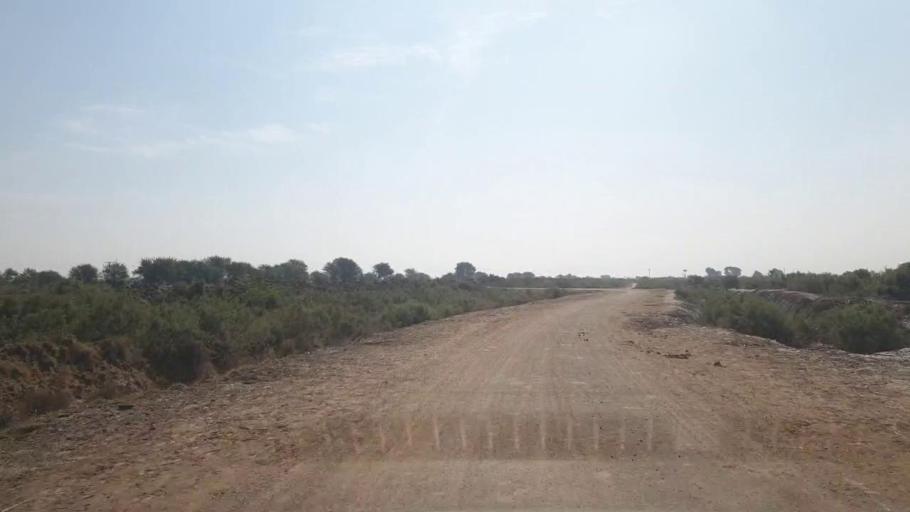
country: PK
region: Sindh
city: Mirwah Gorchani
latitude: 25.3657
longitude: 69.1915
